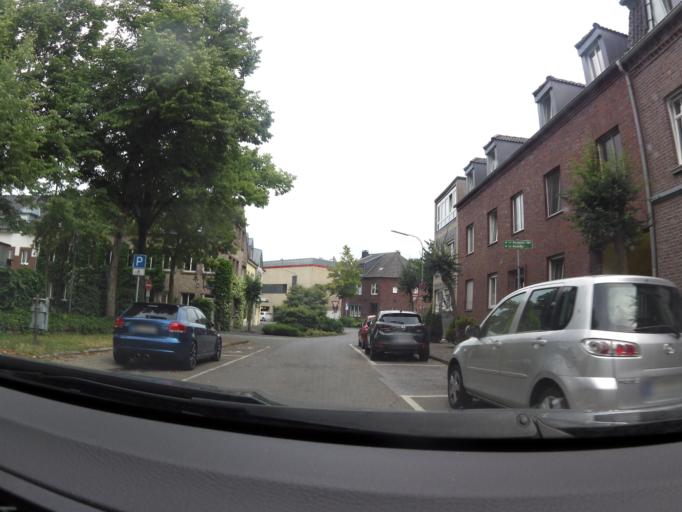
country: DE
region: North Rhine-Westphalia
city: Geldern
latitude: 51.5174
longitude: 6.3192
